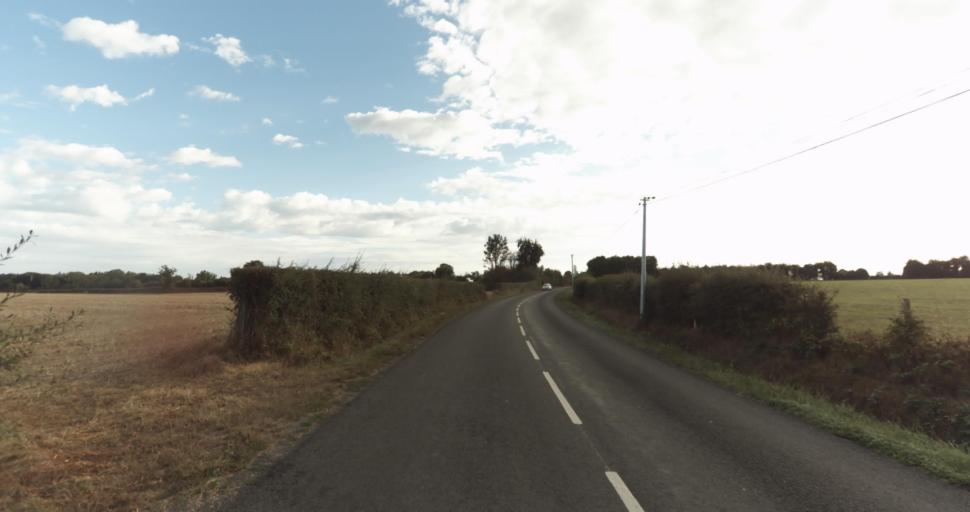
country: FR
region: Lower Normandy
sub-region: Departement de l'Orne
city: Vimoutiers
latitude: 48.9461
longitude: 0.2450
